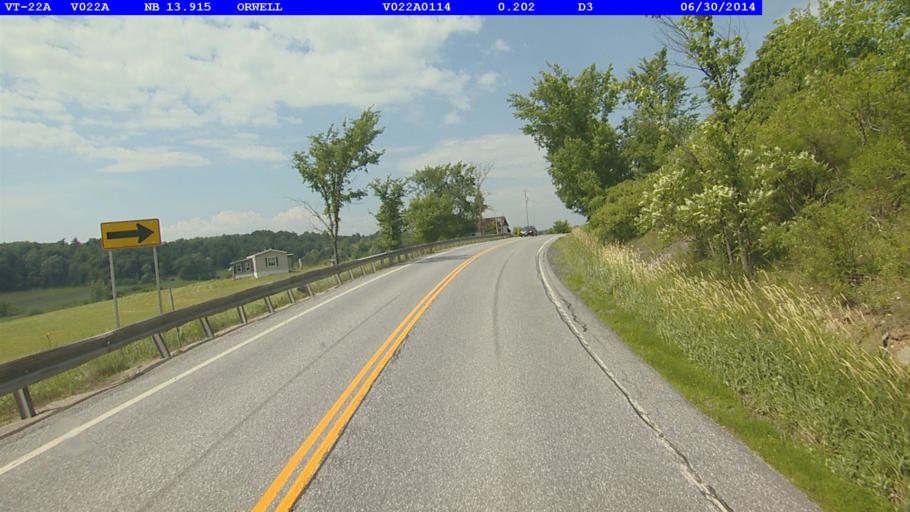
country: US
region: New York
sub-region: Essex County
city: Ticonderoga
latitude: 43.7603
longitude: -73.3125
